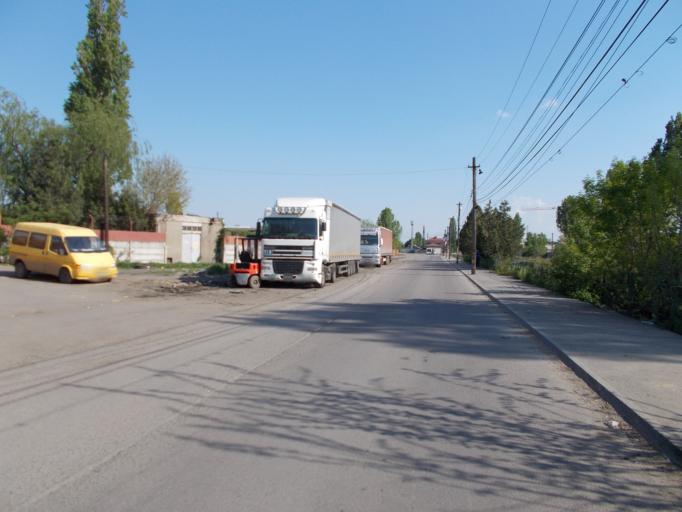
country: RO
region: Ilfov
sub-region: Comuna Jilava
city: Jilava
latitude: 44.3680
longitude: 26.0893
